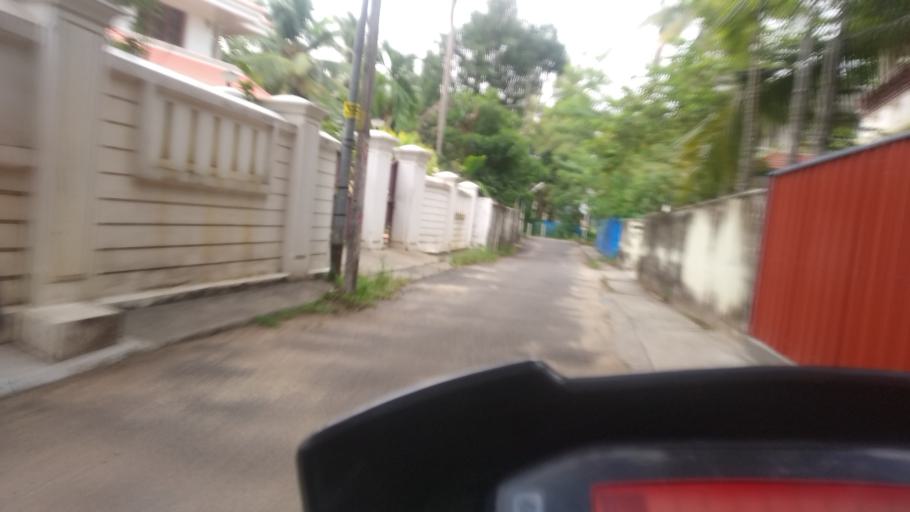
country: IN
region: Kerala
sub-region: Ernakulam
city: Elur
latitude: 10.0690
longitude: 76.2171
